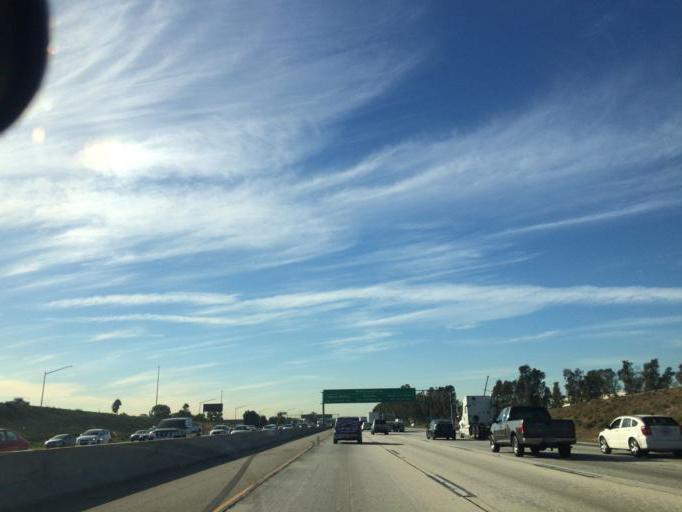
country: US
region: California
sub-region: San Bernardino County
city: Rancho Cucamonga
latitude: 34.0675
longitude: -117.5473
